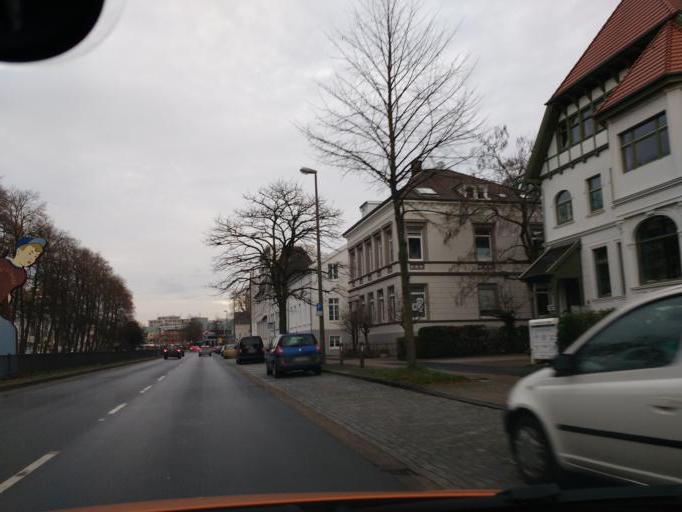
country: DE
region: Lower Saxony
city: Oldenburg
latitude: 53.1410
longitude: 8.2167
